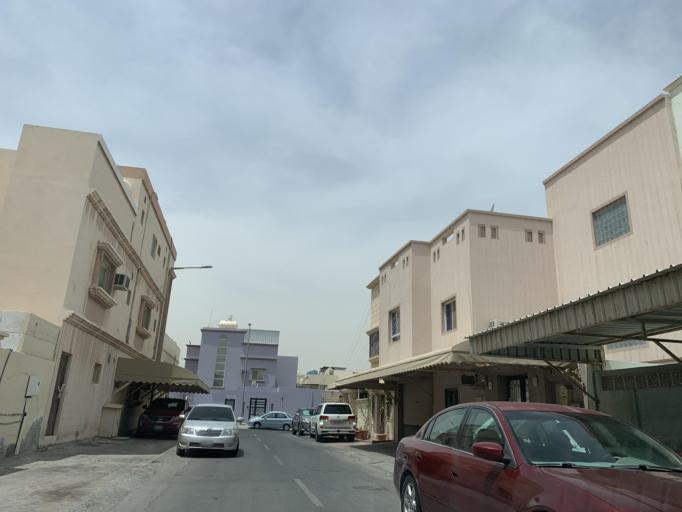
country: BH
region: Northern
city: Madinat `Isa
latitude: 26.1733
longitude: 50.5541
